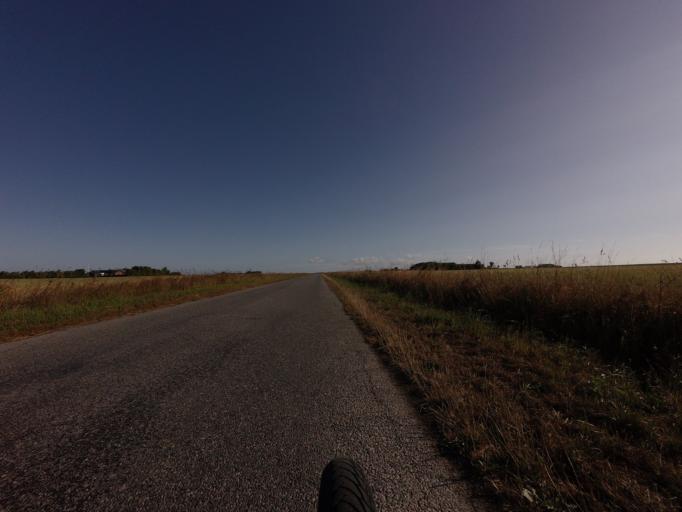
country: DK
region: North Denmark
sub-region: Hjorring Kommune
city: Vra
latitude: 57.3904
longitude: 9.9267
